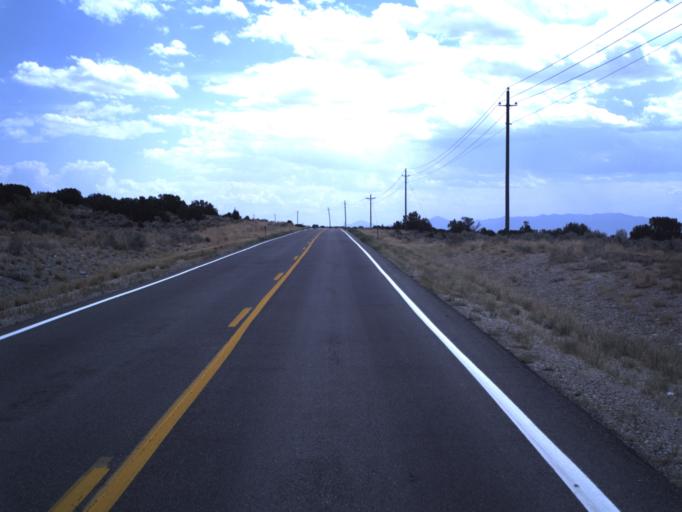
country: US
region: Utah
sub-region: Tooele County
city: Tooele
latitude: 40.3363
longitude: -112.2996
